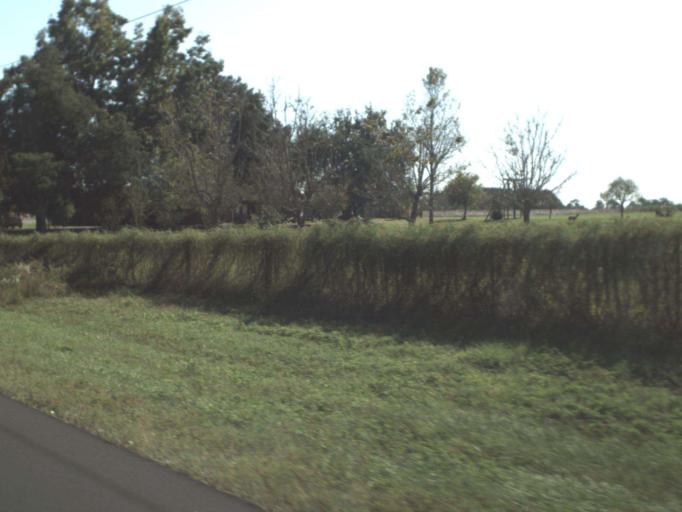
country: US
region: Florida
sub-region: Walton County
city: DeFuniak Springs
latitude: 30.8307
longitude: -86.2316
